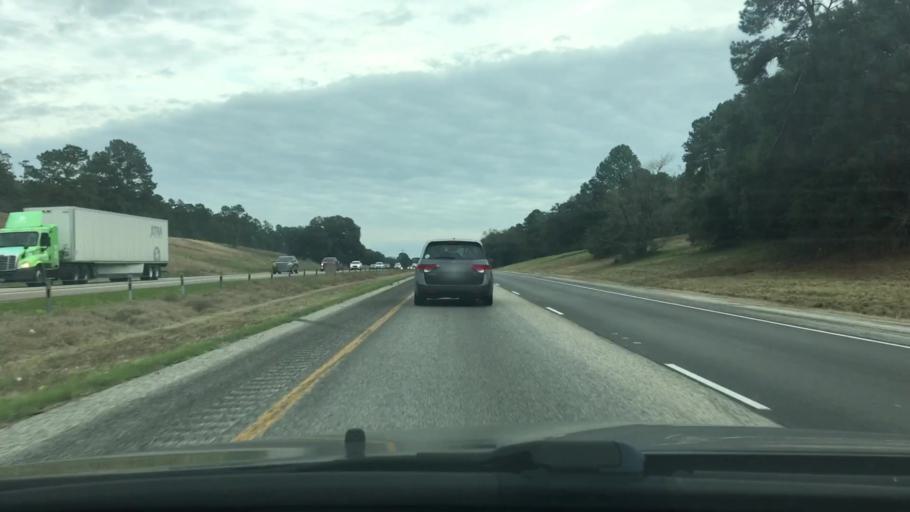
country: US
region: Texas
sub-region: Walker County
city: Huntsville
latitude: 30.8157
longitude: -95.6982
